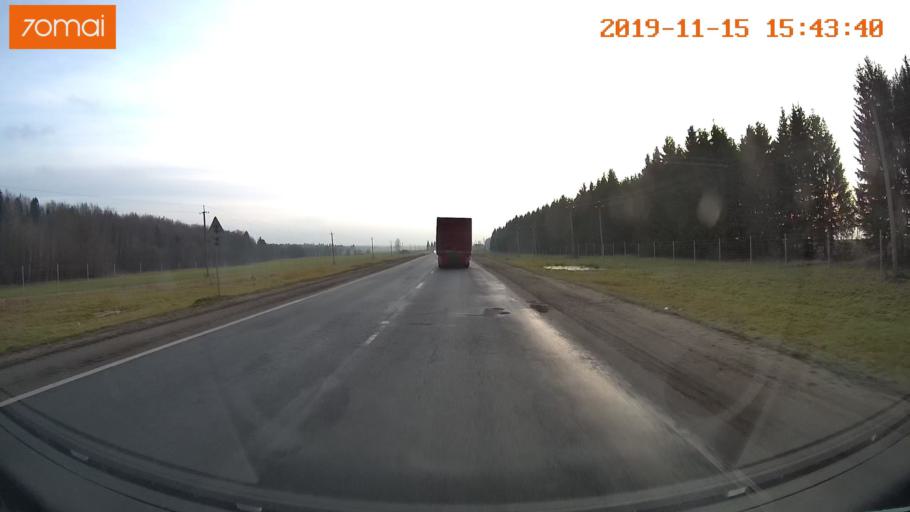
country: RU
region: Jaroslavl
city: Danilov
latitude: 57.9795
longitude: 40.0261
